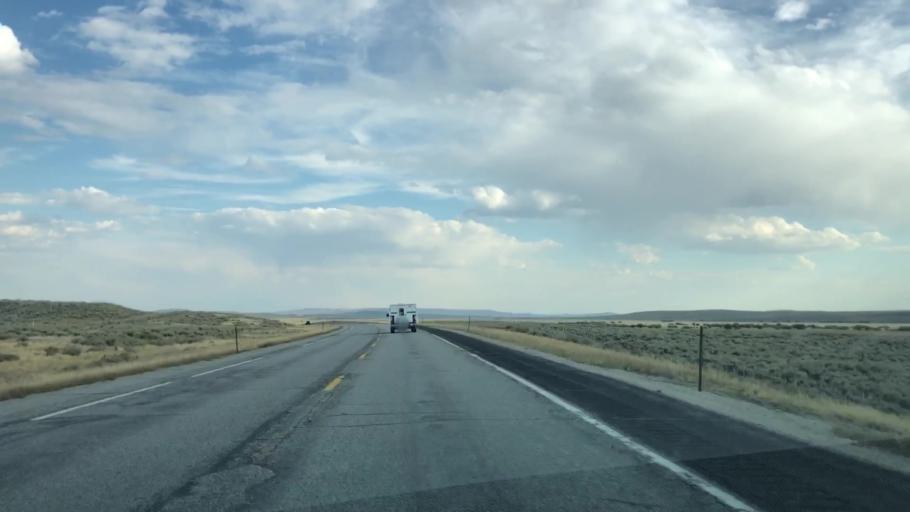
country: US
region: Wyoming
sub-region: Sublette County
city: Pinedale
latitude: 43.0491
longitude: -110.1500
